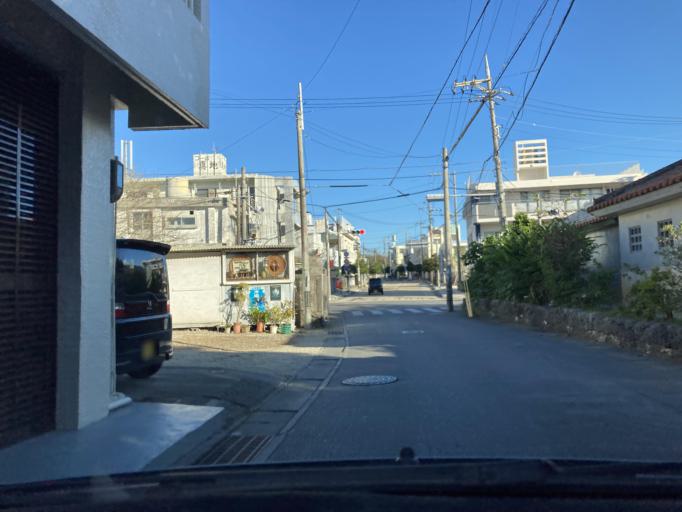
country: JP
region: Okinawa
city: Naha-shi
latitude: 26.2050
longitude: 127.7147
